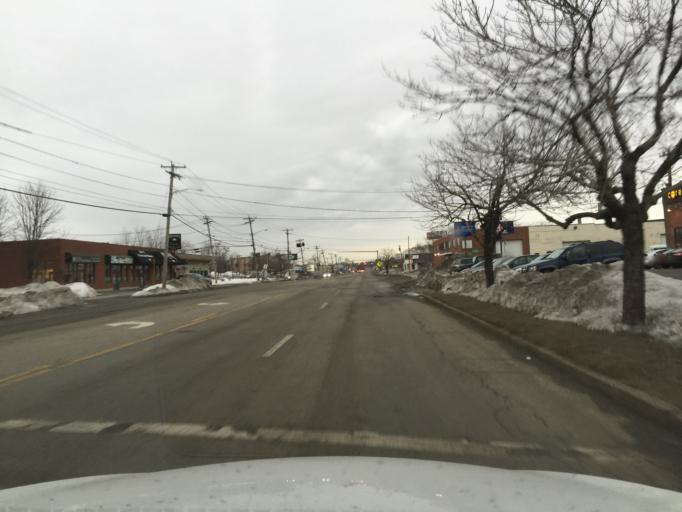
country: US
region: Massachusetts
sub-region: Middlesex County
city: Medford
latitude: 42.4038
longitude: -71.0997
